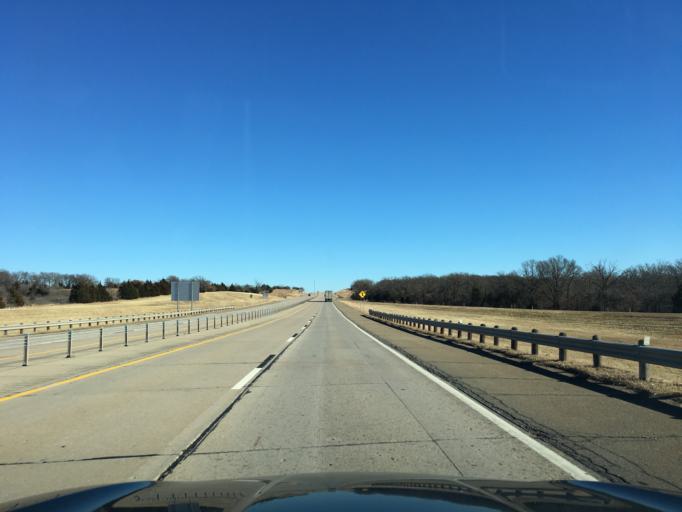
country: US
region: Oklahoma
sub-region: Pawnee County
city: Pawnee
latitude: 36.2248
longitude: -96.7832
